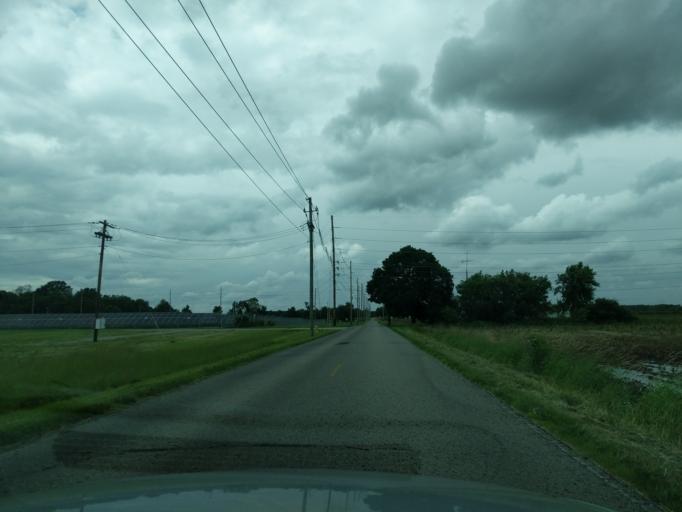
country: US
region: Indiana
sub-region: Madison County
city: Edgewood
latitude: 40.0512
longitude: -85.7302
